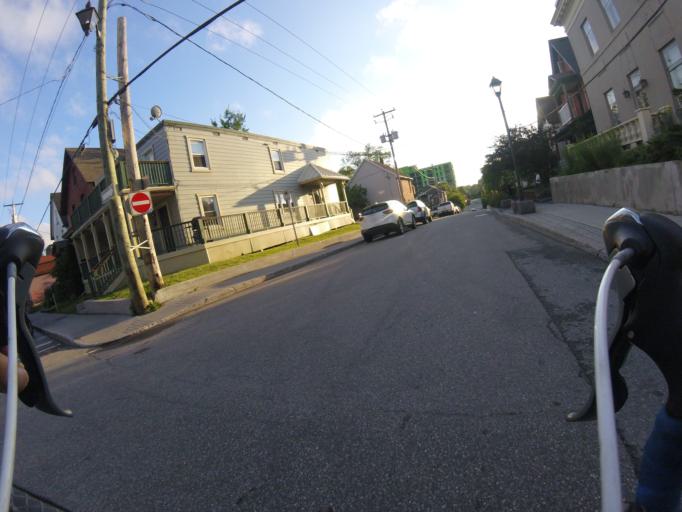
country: CA
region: Ontario
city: Ottawa
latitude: 45.4310
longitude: -75.7110
